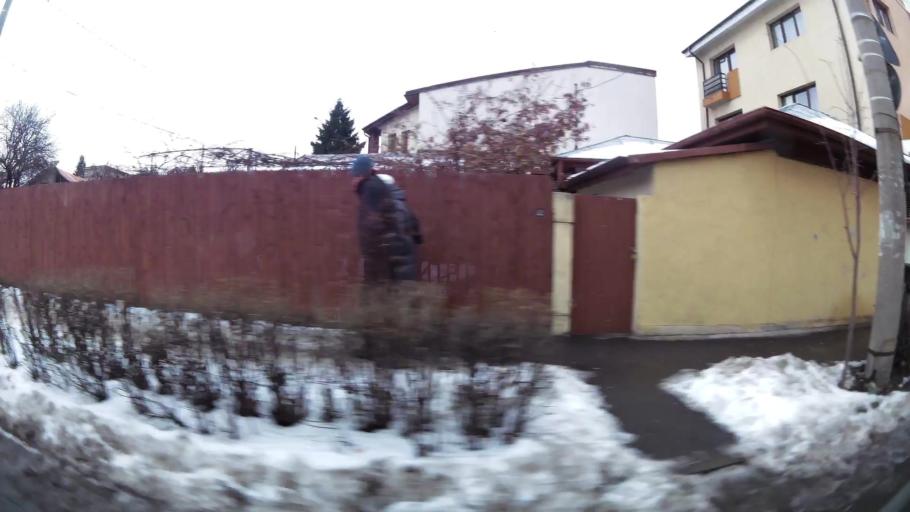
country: RO
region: Ilfov
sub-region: Comuna Pantelimon
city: Pantelimon
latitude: 44.4348
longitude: 26.1955
